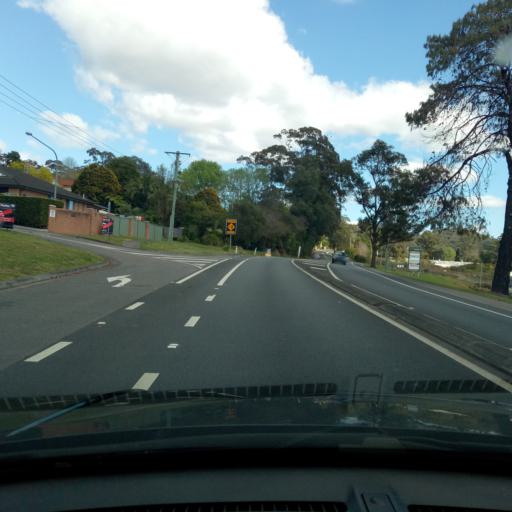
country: AU
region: New South Wales
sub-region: Gosford Shire
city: Lisarow
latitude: -33.3851
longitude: 151.3635
